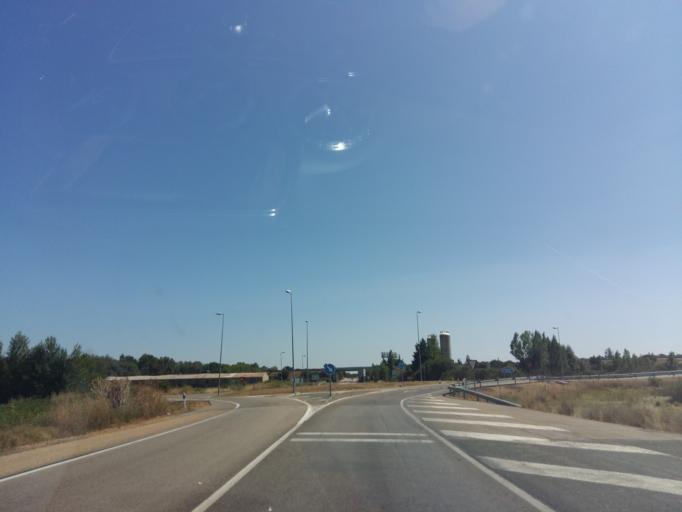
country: ES
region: Castille and Leon
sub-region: Provincia de Leon
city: Astorga
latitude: 42.4413
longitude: -6.0394
